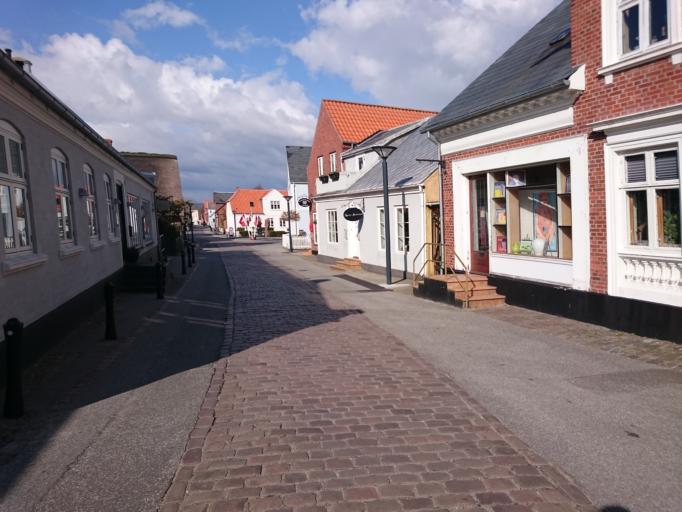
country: DK
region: South Denmark
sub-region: Fano Kommune
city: Nordby
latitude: 55.4454
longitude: 8.4042
